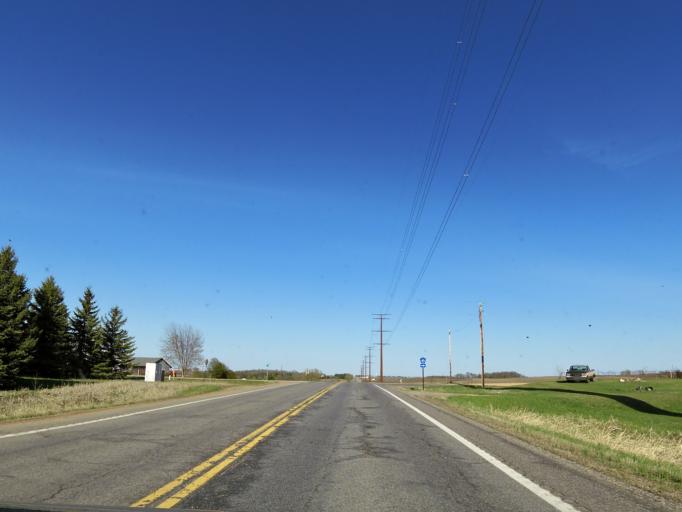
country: US
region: Minnesota
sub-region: Rice County
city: Lonsdale
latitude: 44.5727
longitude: -93.4210
